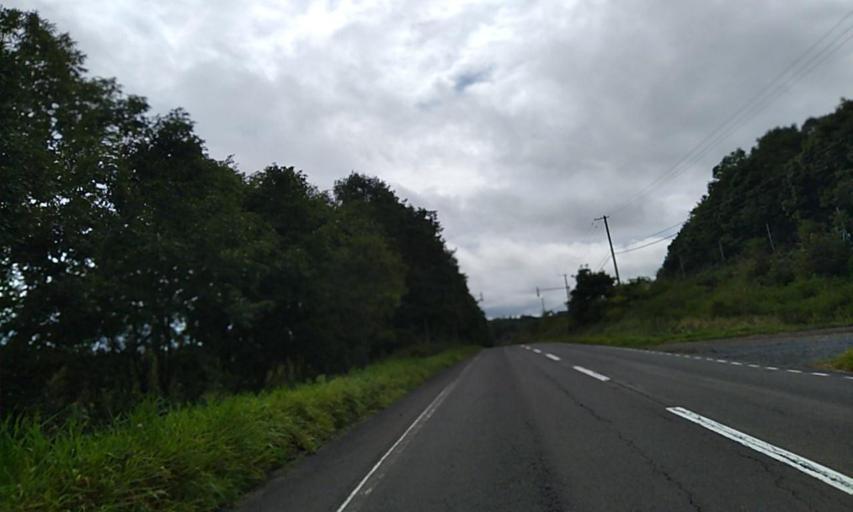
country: JP
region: Hokkaido
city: Shibetsu
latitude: 43.3247
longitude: 145.2153
